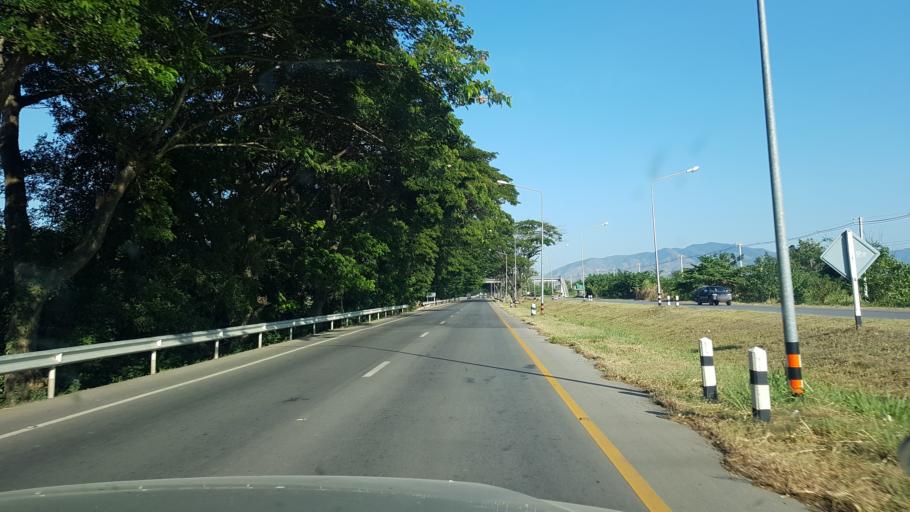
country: TH
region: Phetchabun
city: Lom Sak
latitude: 16.7272
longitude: 101.2594
